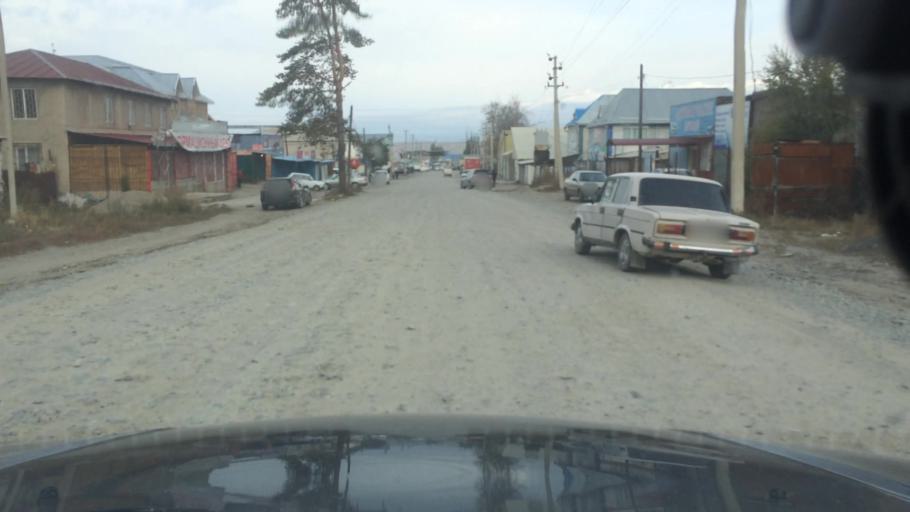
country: KG
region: Ysyk-Koel
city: Karakol
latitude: 42.4902
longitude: 78.3880
